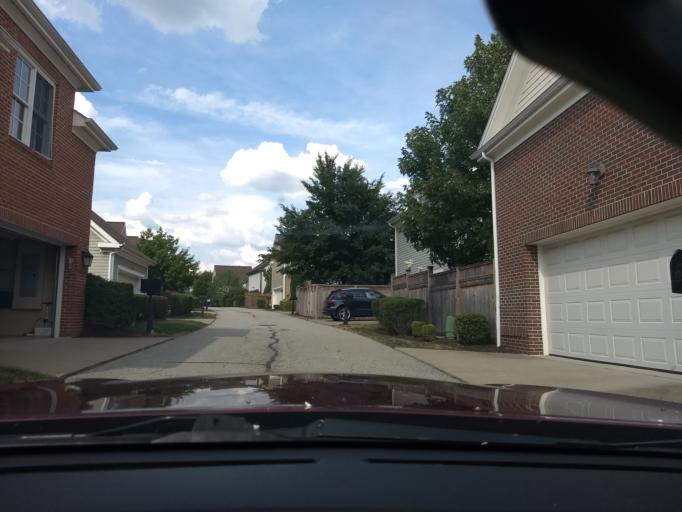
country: US
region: Pennsylvania
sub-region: Allegheny County
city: Homestead
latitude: 40.4180
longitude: -79.9181
